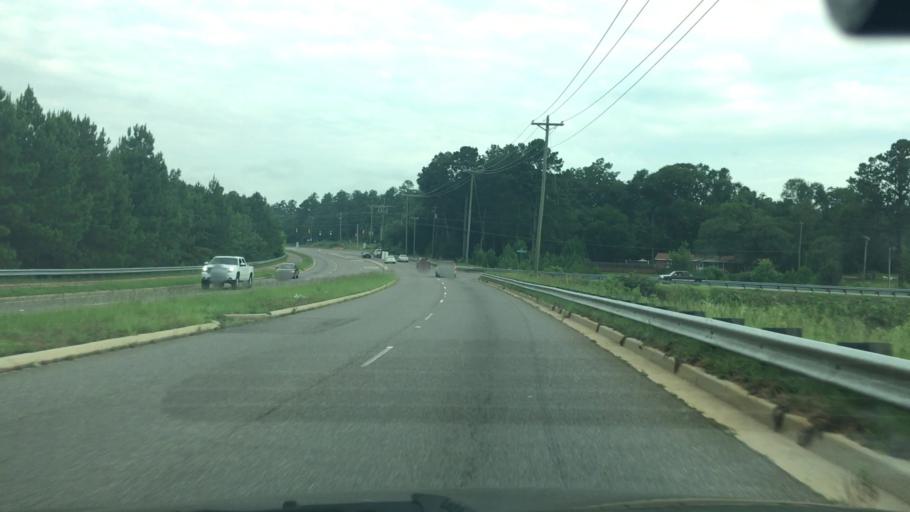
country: US
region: South Carolina
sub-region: Aiken County
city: Aiken
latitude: 33.5707
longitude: -81.6911
